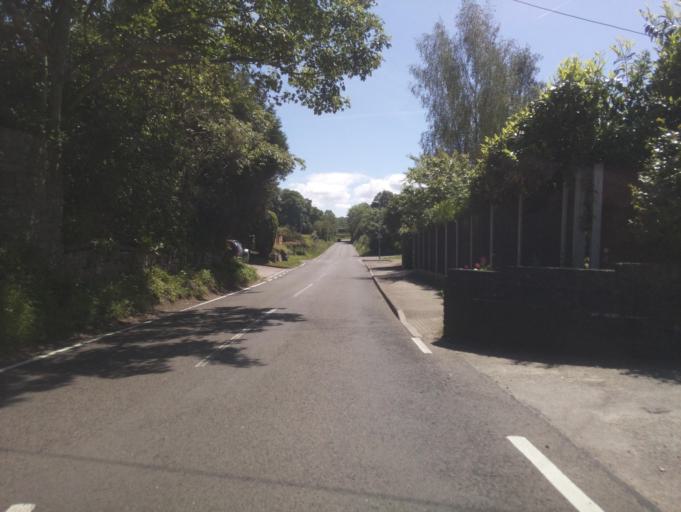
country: GB
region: Wales
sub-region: Monmouthshire
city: Caldicot
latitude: 51.6077
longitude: -2.7411
